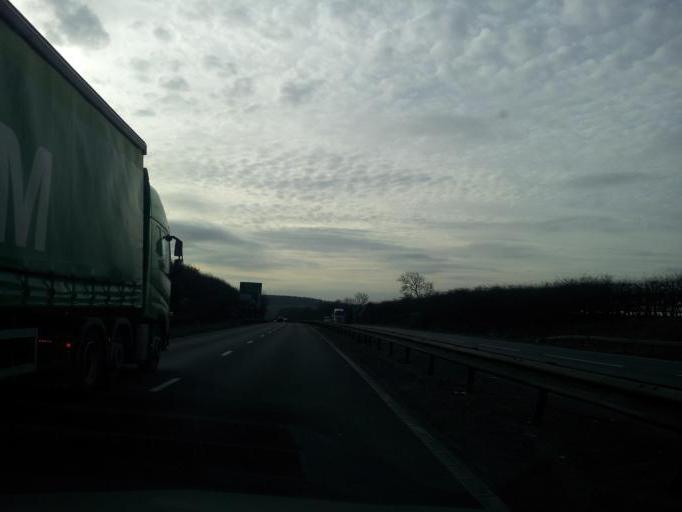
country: GB
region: England
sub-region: District of Rutland
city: Tinwell
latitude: 52.6519
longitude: -0.5106
